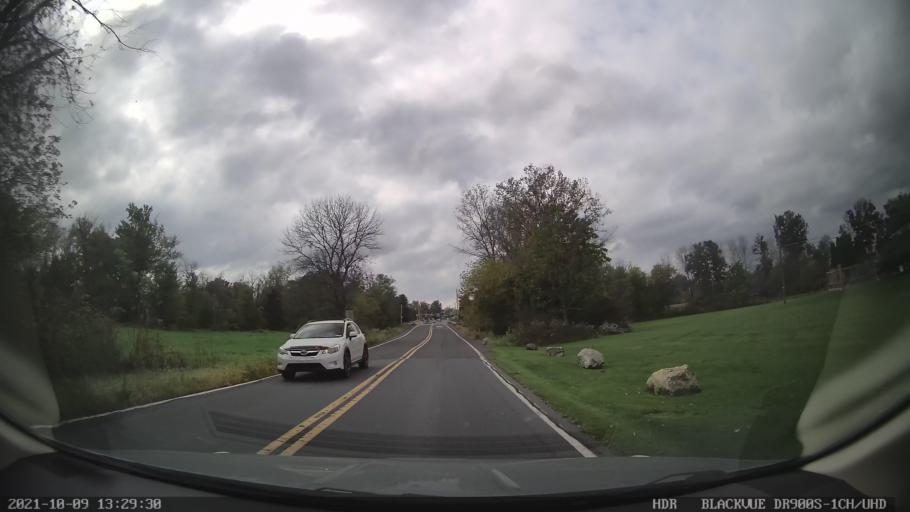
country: US
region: Pennsylvania
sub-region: Lehigh County
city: Trexlertown
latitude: 40.5350
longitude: -75.5998
